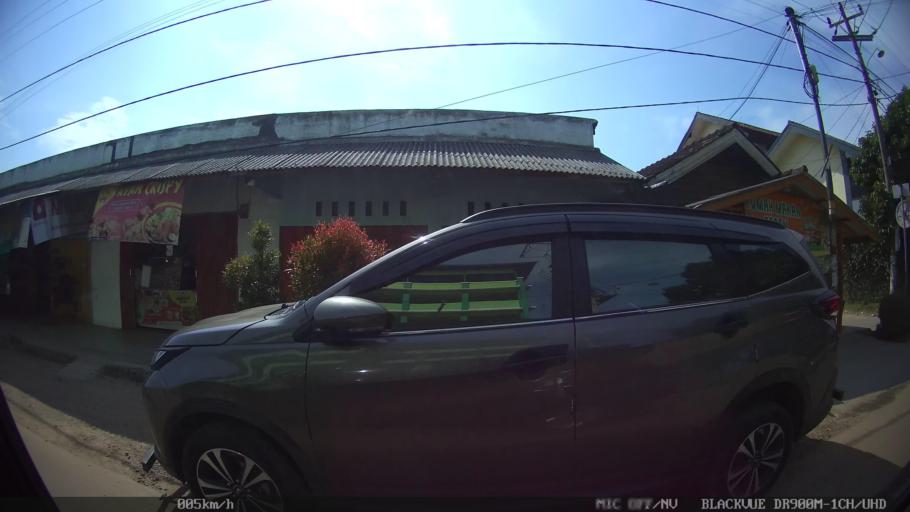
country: ID
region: Lampung
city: Kedaton
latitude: -5.3742
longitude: 105.2382
